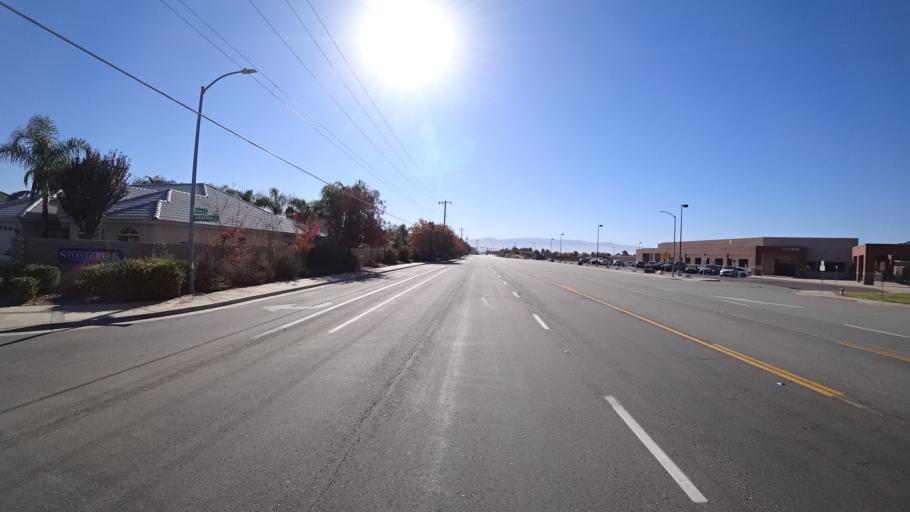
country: US
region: California
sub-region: Kern County
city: Greenfield
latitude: 35.2773
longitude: -119.0566
